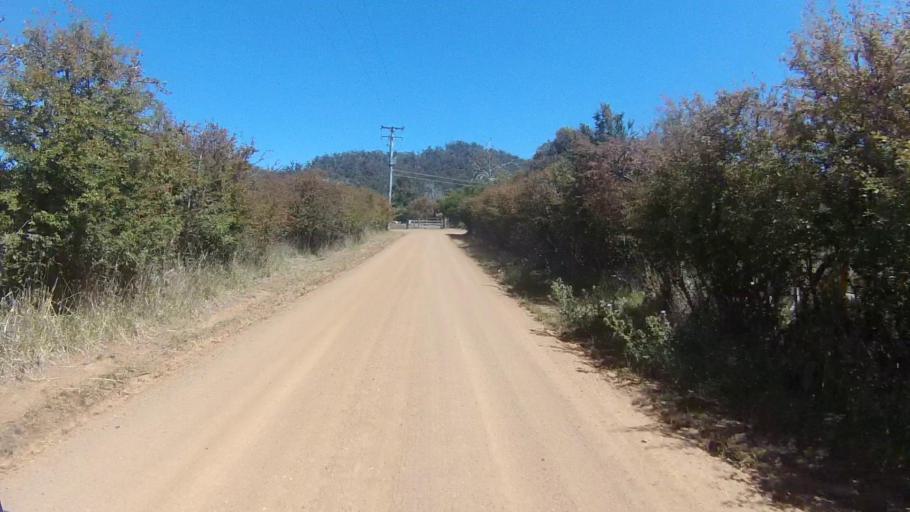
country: AU
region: Tasmania
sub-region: Clarence
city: Cambridge
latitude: -42.8463
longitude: 147.4571
